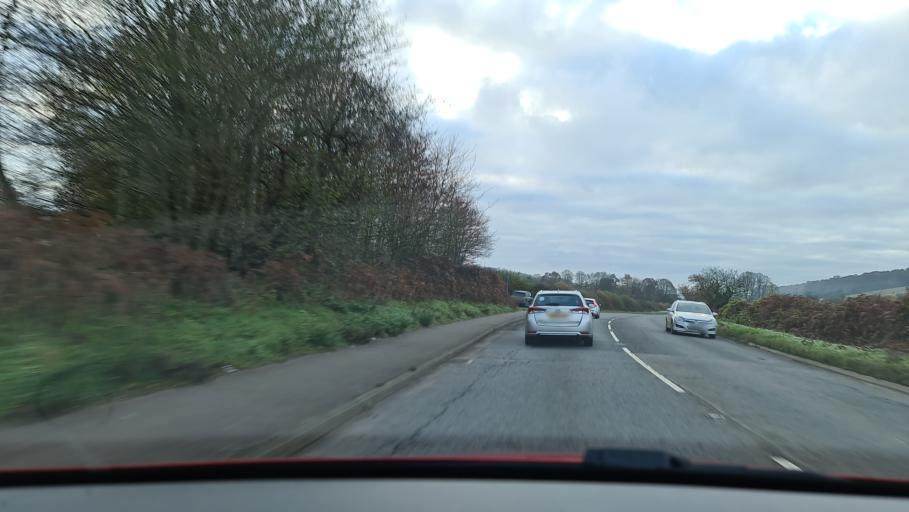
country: GB
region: England
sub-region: Buckinghamshire
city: Princes Risborough
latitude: 51.6697
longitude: -0.8136
